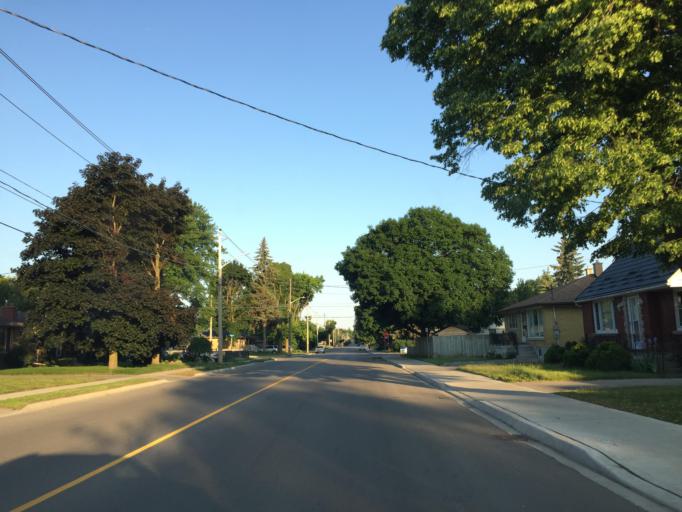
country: CA
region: Ontario
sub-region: Wellington County
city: Guelph
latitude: 43.5626
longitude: -80.2574
